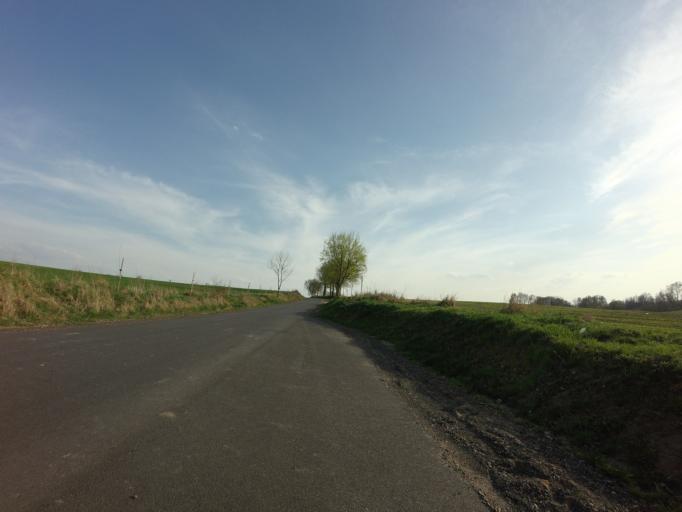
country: PL
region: West Pomeranian Voivodeship
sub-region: Powiat choszczenski
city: Choszczno
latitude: 53.1826
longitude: 15.4997
